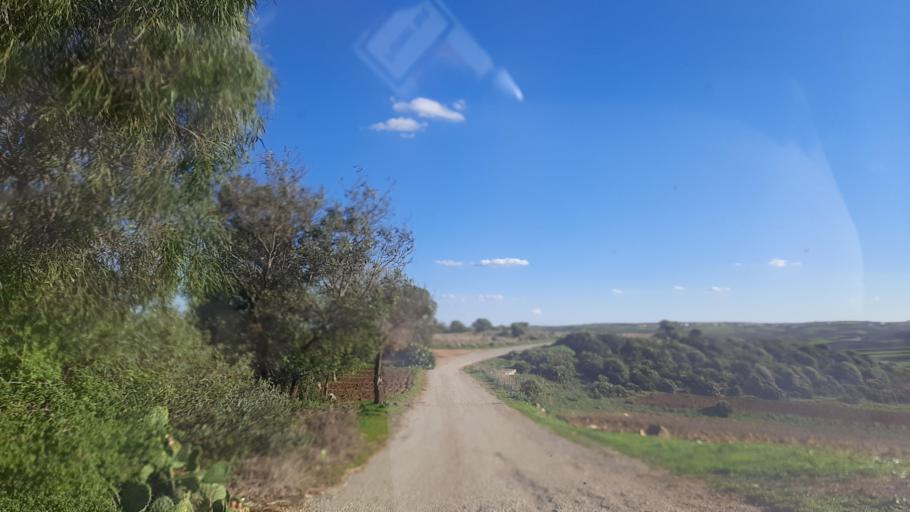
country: TN
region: Nabul
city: El Mida
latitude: 36.8364
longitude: 10.8337
